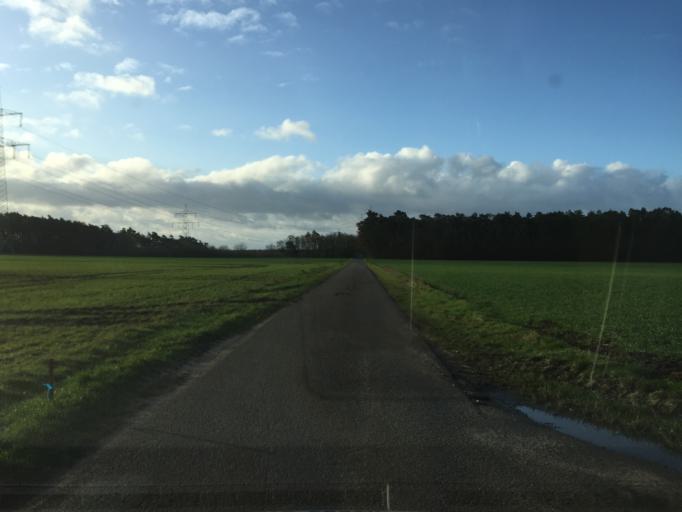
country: DE
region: Lower Saxony
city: Steyerberg
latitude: 52.6028
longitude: 8.9875
